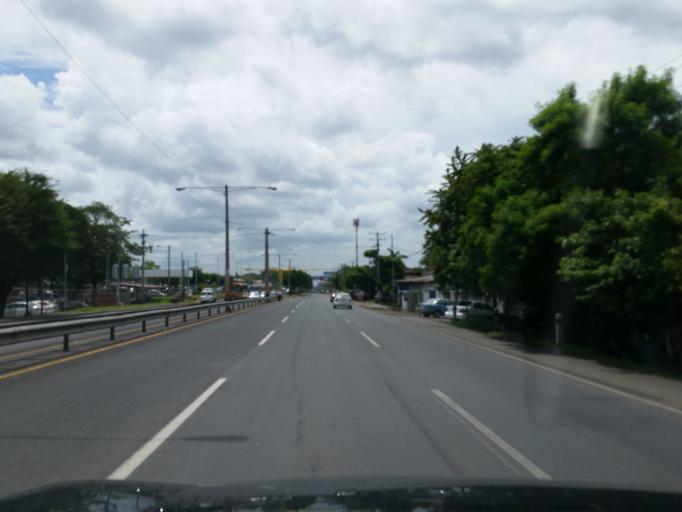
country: NI
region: Managua
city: Managua
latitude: 12.1452
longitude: -86.1685
